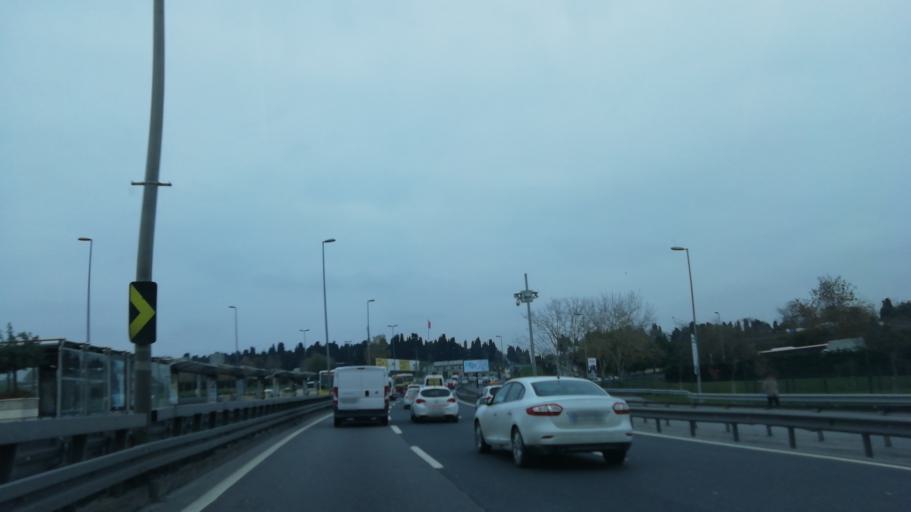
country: TR
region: Istanbul
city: Istanbul
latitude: 41.0299
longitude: 28.9248
